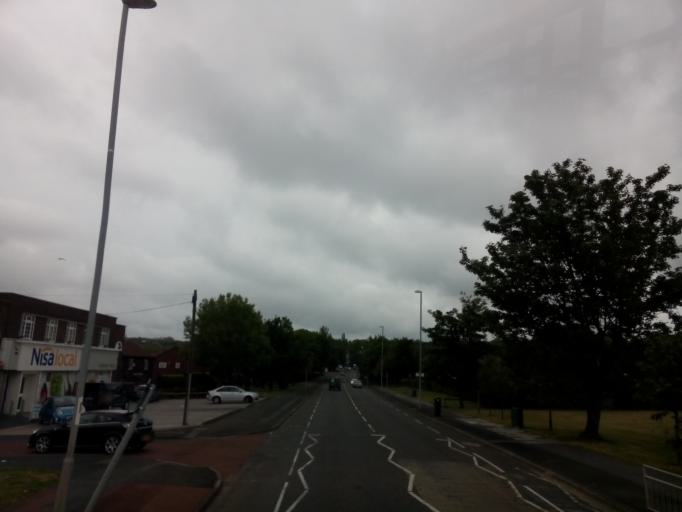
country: GB
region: England
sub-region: Gateshead
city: Lamesley
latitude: 54.9029
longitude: -1.5782
